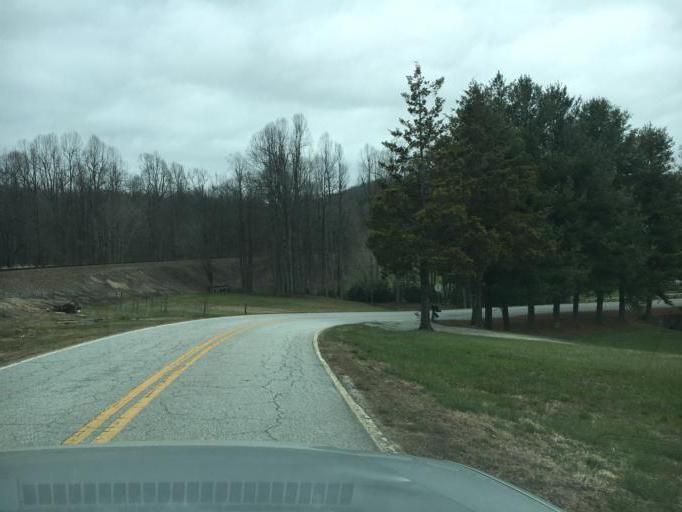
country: US
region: North Carolina
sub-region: Henderson County
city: East Flat Rock
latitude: 35.2471
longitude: -82.4148
